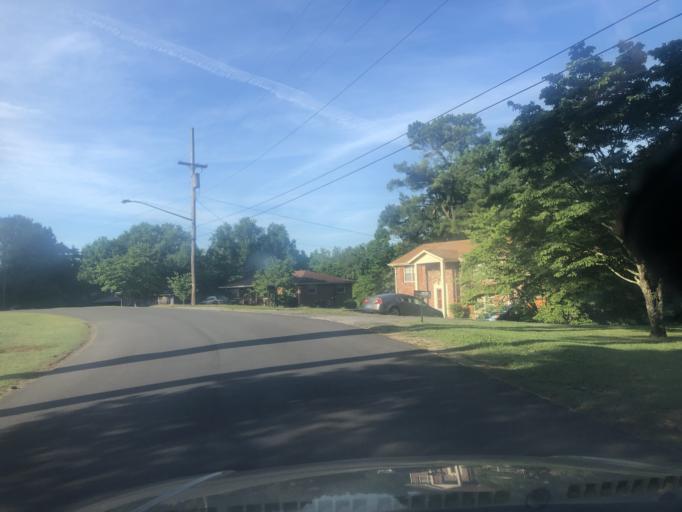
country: US
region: Tennessee
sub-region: Davidson County
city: Lakewood
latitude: 36.2516
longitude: -86.6518
